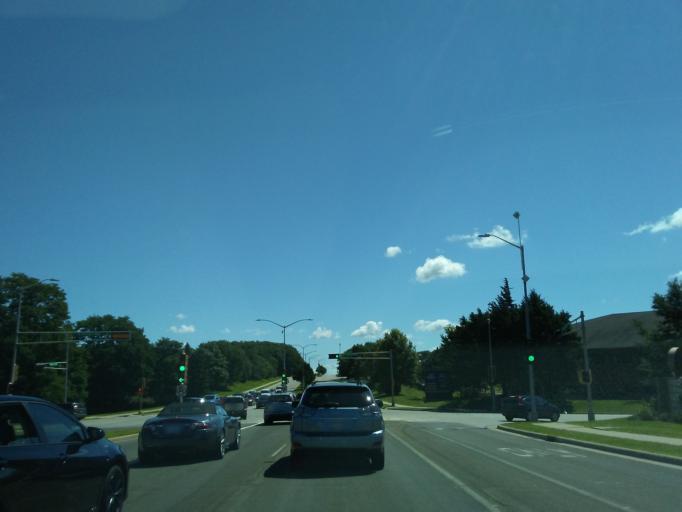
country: US
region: Wisconsin
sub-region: Dane County
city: Fitchburg
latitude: 43.0153
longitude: -89.4562
